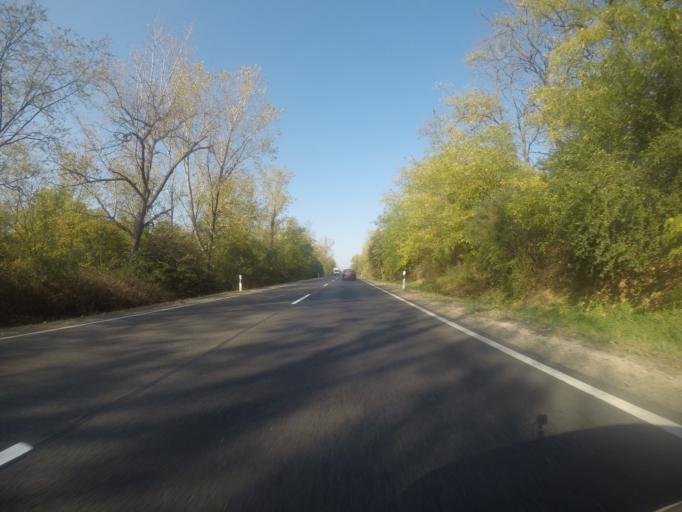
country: HU
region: Fejer
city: Baracs
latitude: 46.8762
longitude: 18.9185
